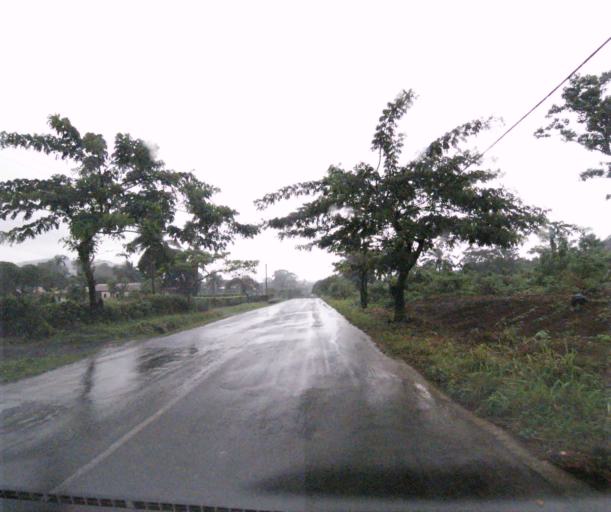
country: CM
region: South-West Province
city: Limbe
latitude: 4.0175
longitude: 9.1855
